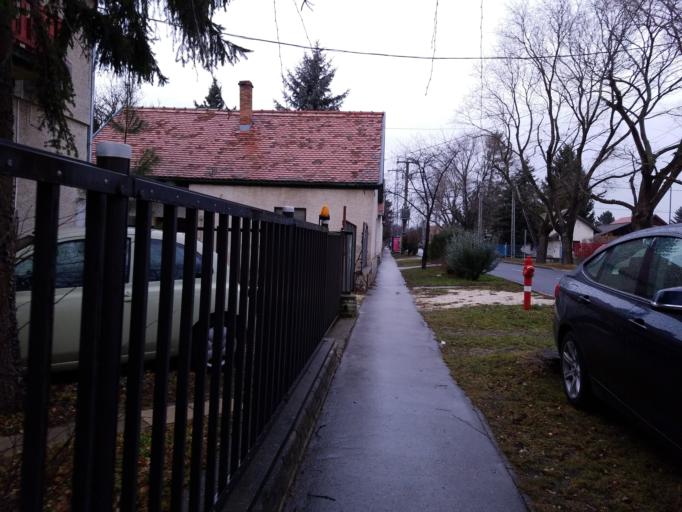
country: HU
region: Pest
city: Toeroekbalint
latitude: 47.4345
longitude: 18.9114
